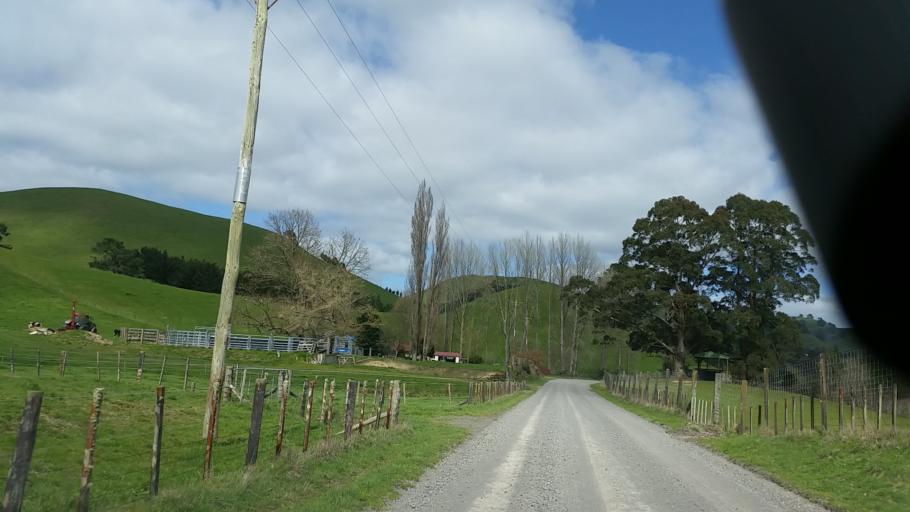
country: NZ
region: Bay of Plenty
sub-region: Rotorua District
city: Rotorua
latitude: -38.3722
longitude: 176.2066
